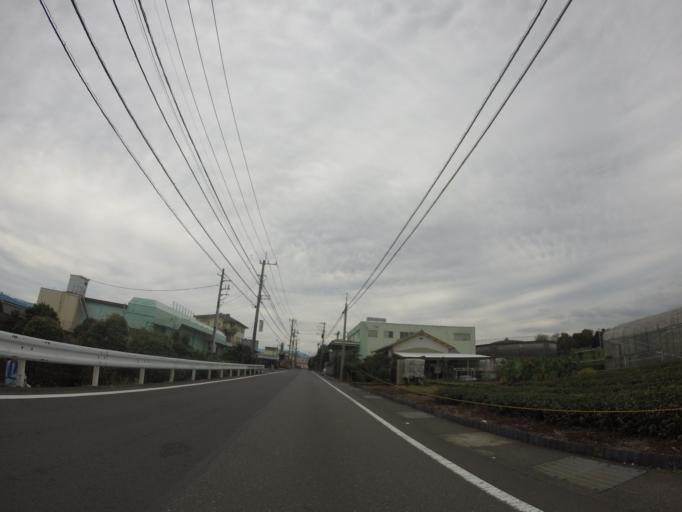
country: JP
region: Shizuoka
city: Fuji
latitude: 35.1967
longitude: 138.6782
